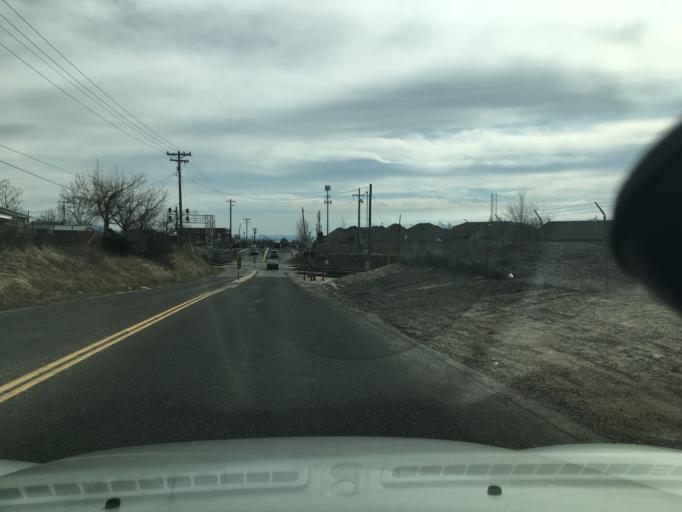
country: US
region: Utah
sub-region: Davis County
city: Clearfield
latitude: 41.0864
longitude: -112.0069
